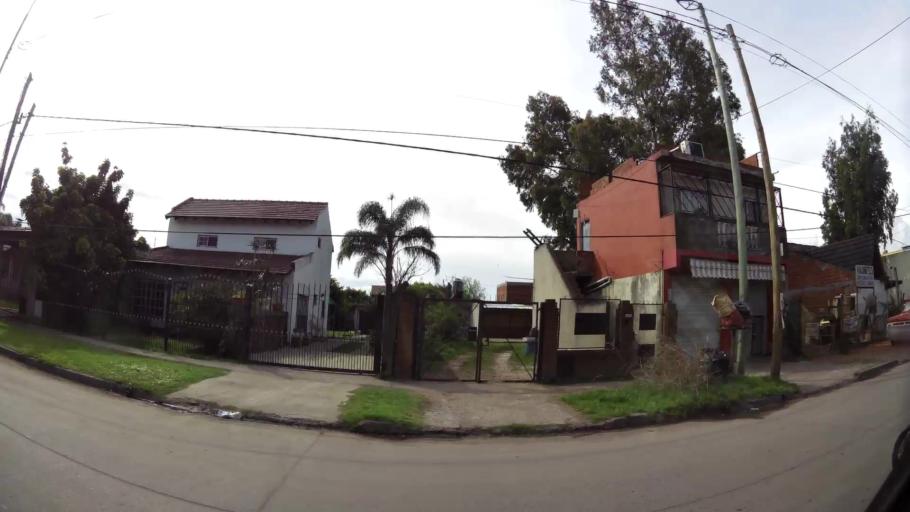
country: AR
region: Buenos Aires
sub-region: Partido de Quilmes
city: Quilmes
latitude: -34.7710
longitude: -58.2623
